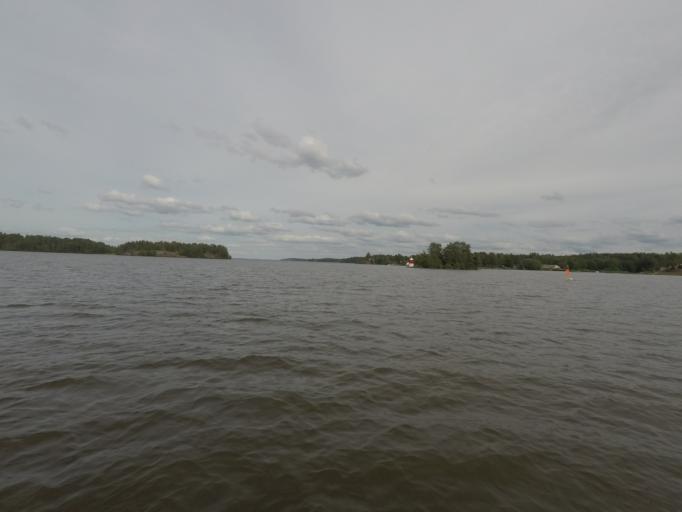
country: SE
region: Soedermanland
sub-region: Eskilstuna Kommun
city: Kvicksund
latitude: 59.4555
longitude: 16.3568
